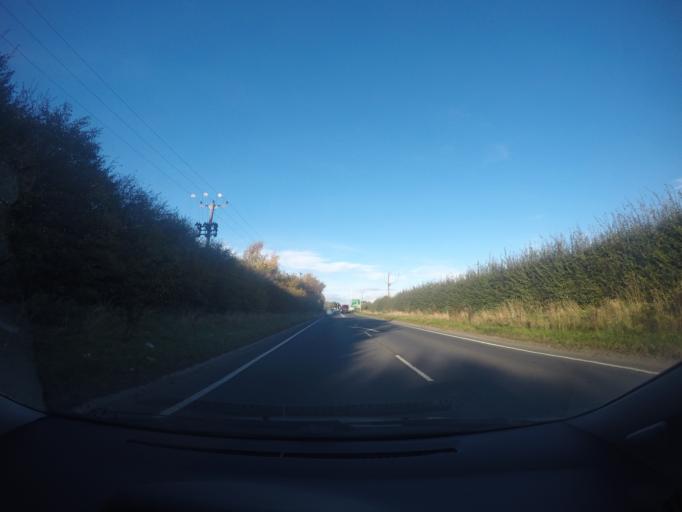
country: GB
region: England
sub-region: City of York
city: Nether Poppleton
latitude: 53.9694
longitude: -1.1455
